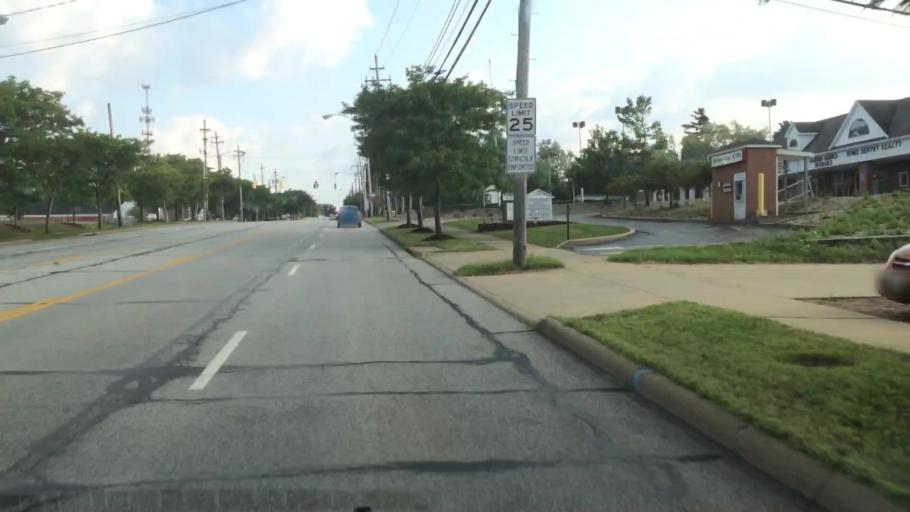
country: US
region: Ohio
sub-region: Cuyahoga County
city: Broadview Heights
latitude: 41.3509
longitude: -81.6855
